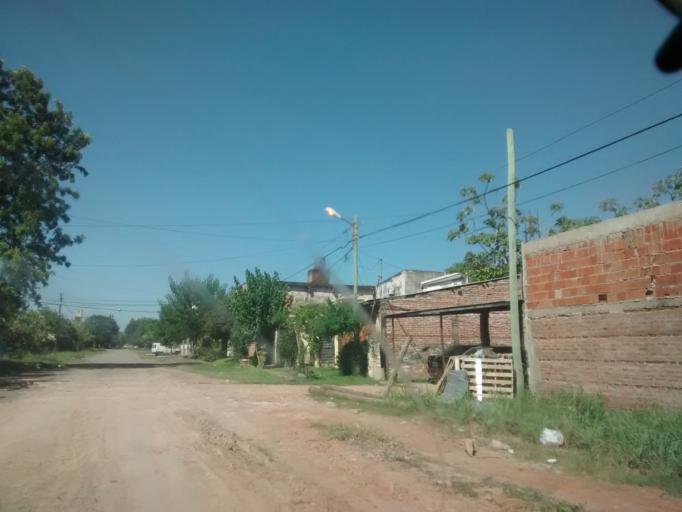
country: AR
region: Chaco
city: Resistencia
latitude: -27.4412
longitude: -58.9736
